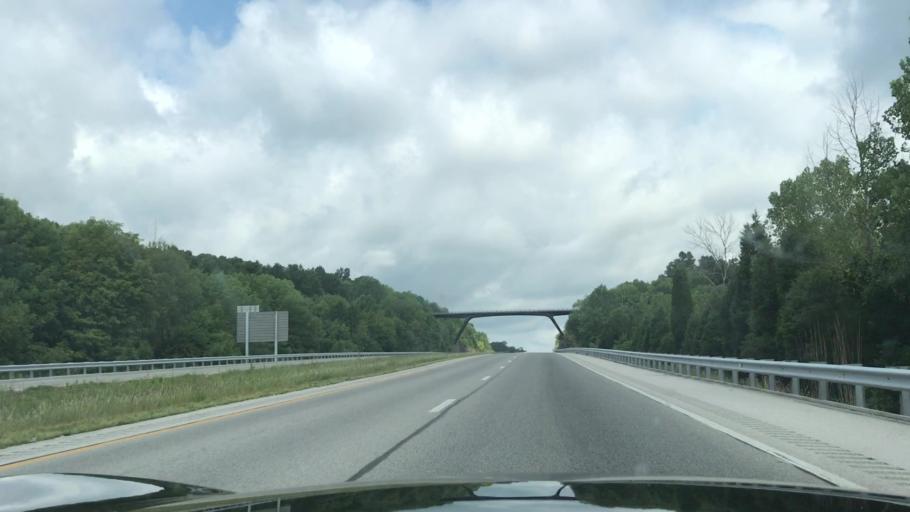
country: US
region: Kentucky
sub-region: Warren County
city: Bowling Green
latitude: 37.0171
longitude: -86.5208
